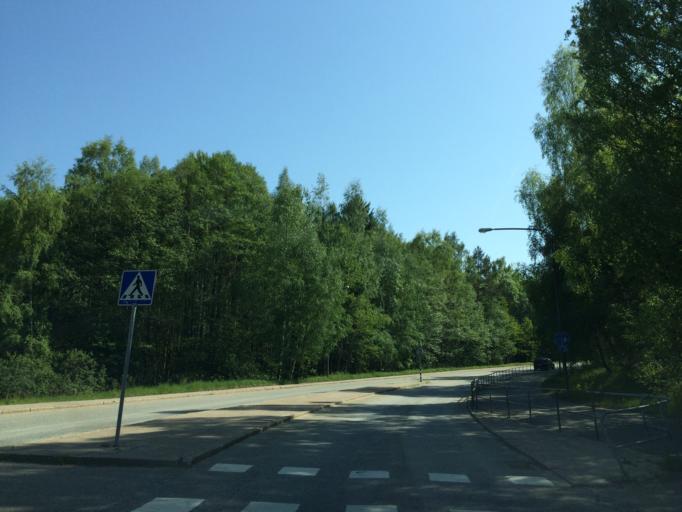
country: SE
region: Stockholm
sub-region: Nacka Kommun
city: Alta
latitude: 59.2575
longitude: 18.1653
